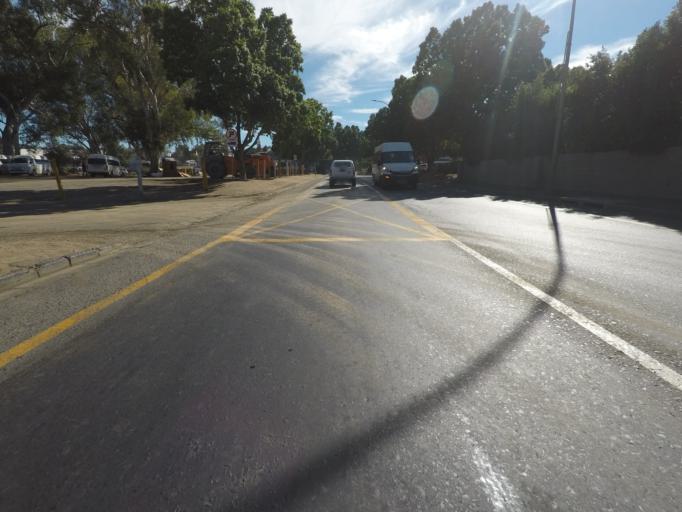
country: ZA
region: Western Cape
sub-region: West Coast District Municipality
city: Malmesbury
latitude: -33.4674
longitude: 18.7282
